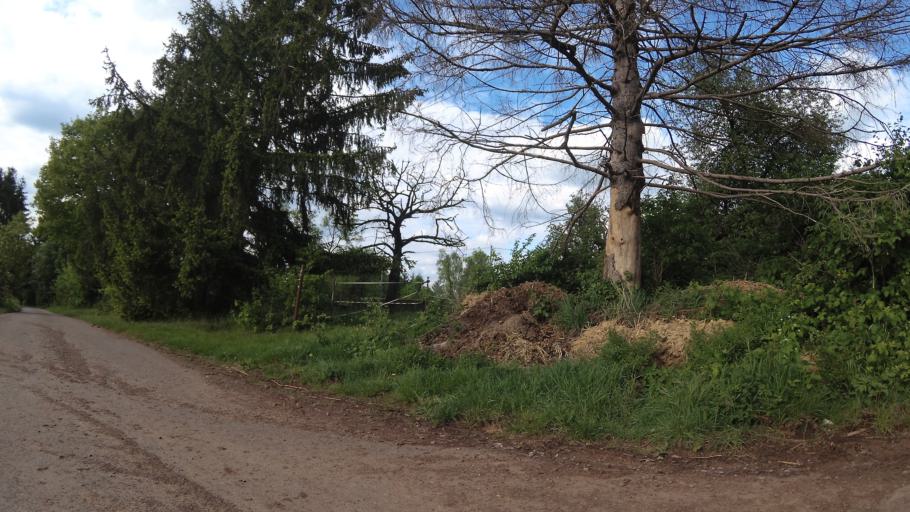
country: DE
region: Saarland
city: Neunkirchen
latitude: 49.3609
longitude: 7.1872
